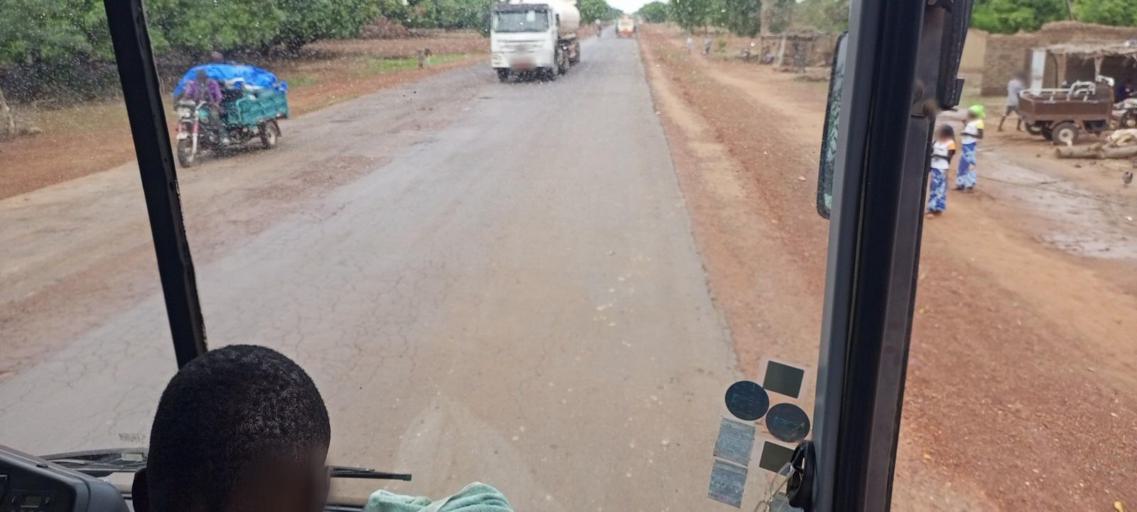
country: ML
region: Sikasso
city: Koutiala
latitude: 12.5810
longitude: -5.6111
